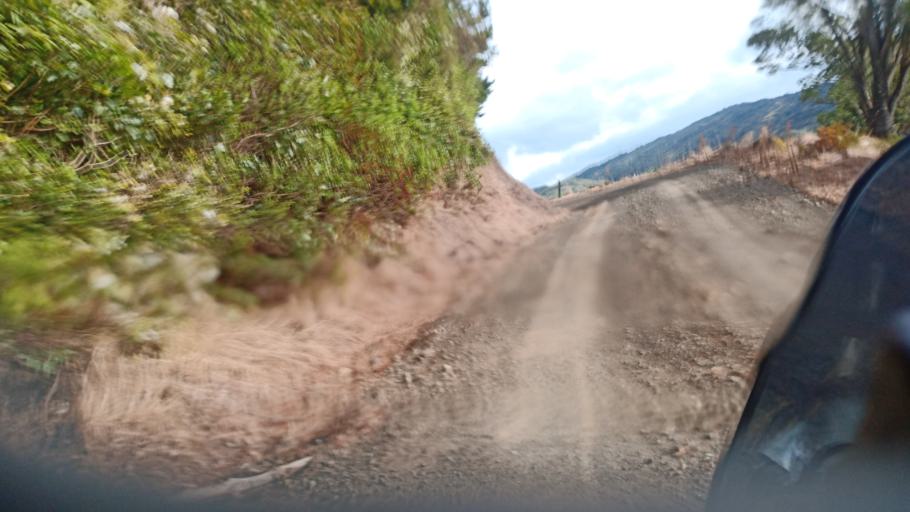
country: NZ
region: Gisborne
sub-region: Gisborne District
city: Gisborne
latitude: -38.4579
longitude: 177.5390
